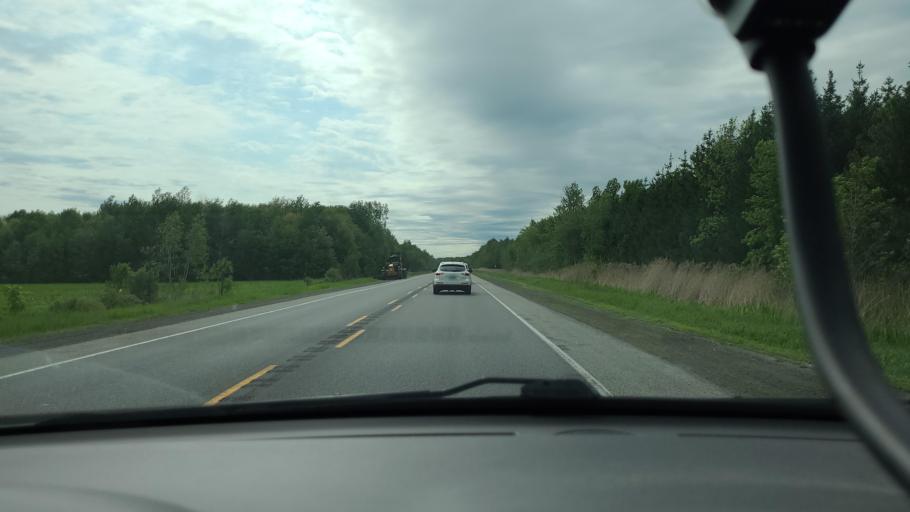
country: CA
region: Quebec
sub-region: Lanaudiere
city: Saint-Jacques
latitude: 45.9645
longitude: -73.5192
